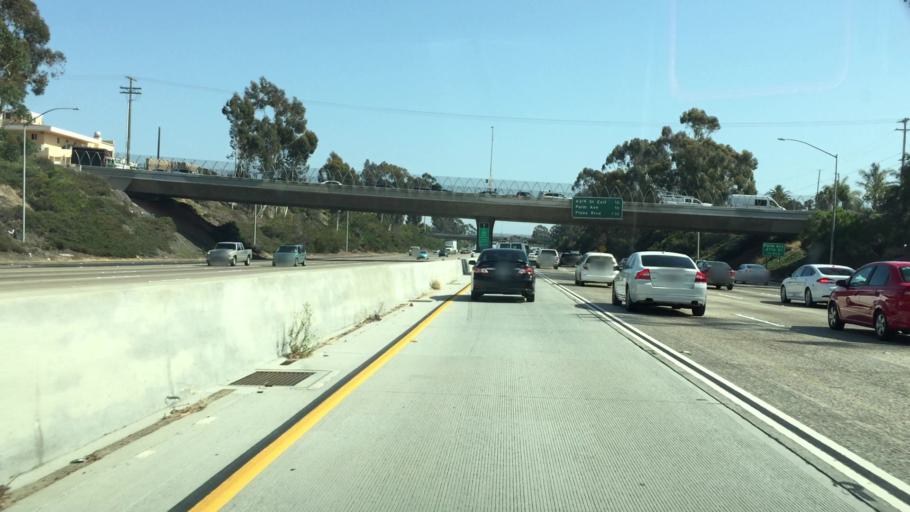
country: US
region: California
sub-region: San Diego County
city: National City
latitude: 32.7015
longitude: -117.0949
